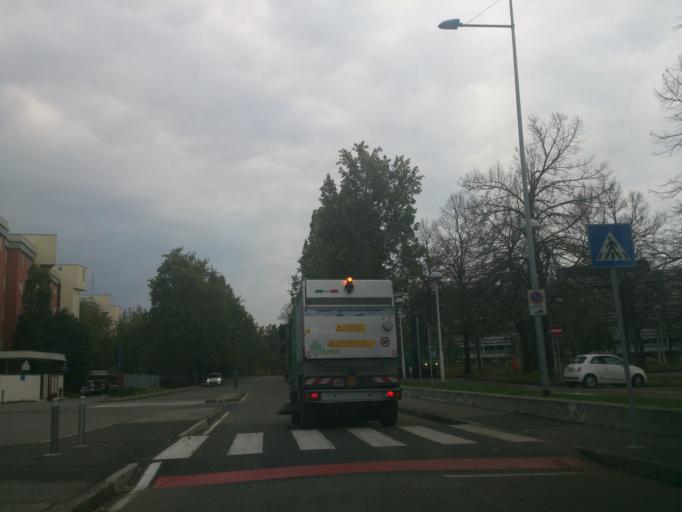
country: IT
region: Lombardy
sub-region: Citta metropolitana di Milano
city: San Donato Milanese
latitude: 45.4180
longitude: 9.2693
